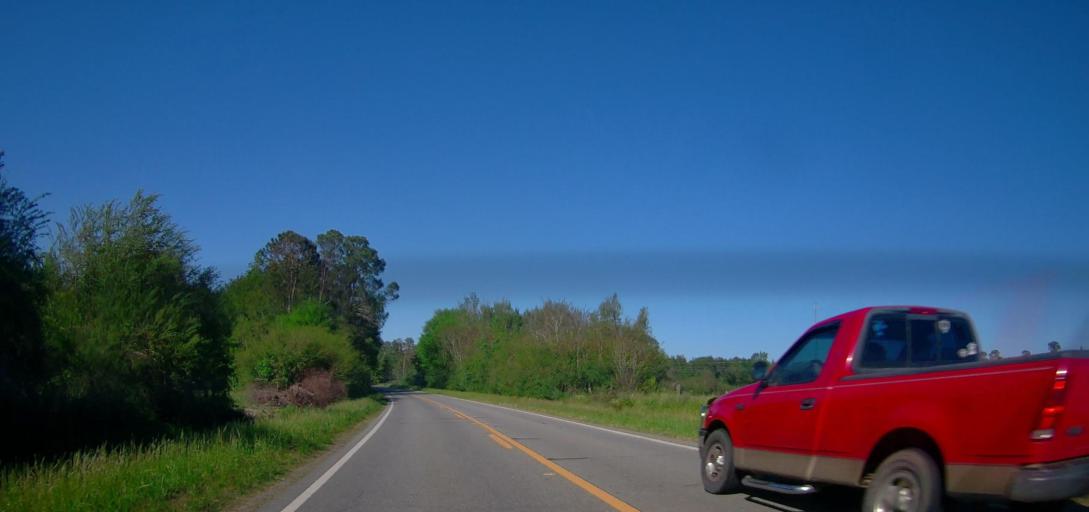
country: US
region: Georgia
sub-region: Wilcox County
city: Rochelle
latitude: 31.9305
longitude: -83.4609
